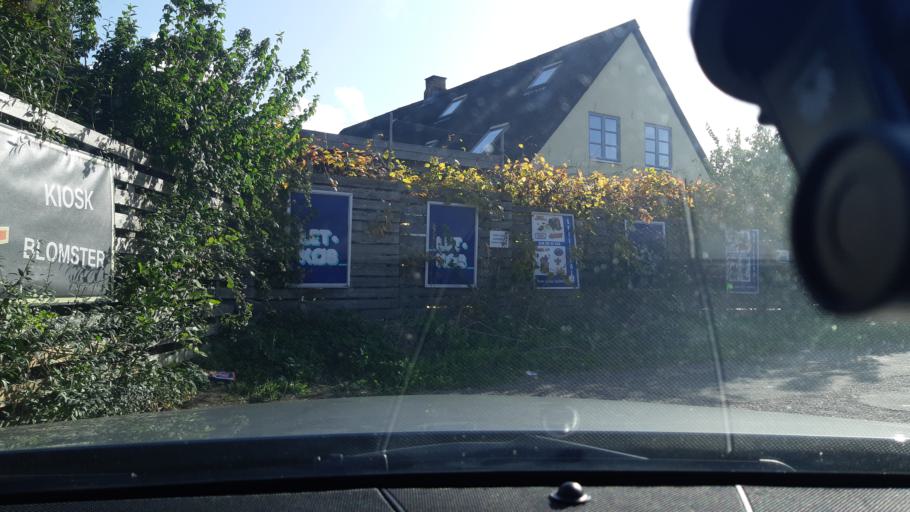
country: DK
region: Zealand
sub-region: Holbaek Kommune
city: Holbaek
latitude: 55.7165
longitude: 11.6880
